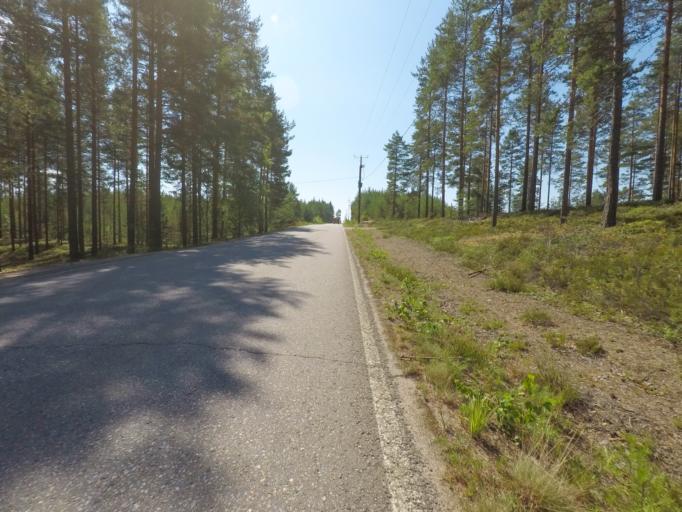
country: FI
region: Southern Savonia
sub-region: Mikkeli
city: Puumala
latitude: 61.4567
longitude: 28.1742
